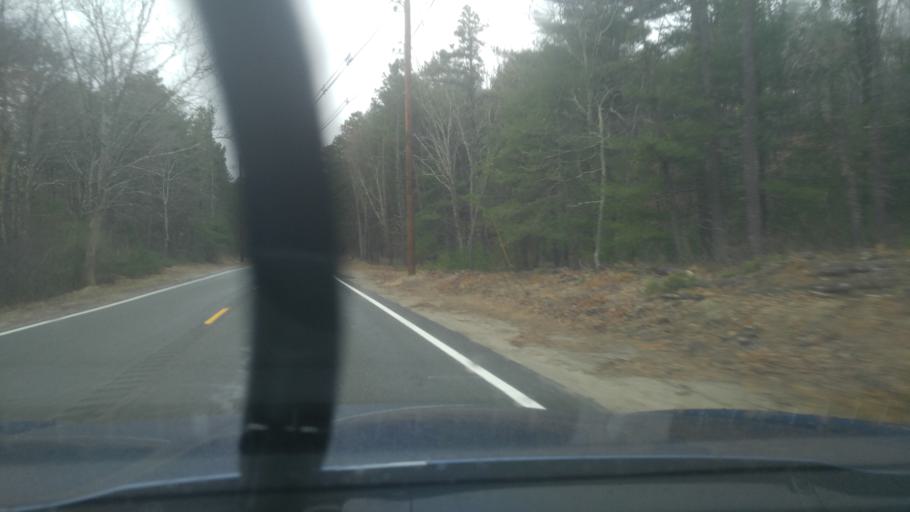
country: US
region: Rhode Island
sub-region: Kent County
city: West Warwick
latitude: 41.6481
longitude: -71.5790
